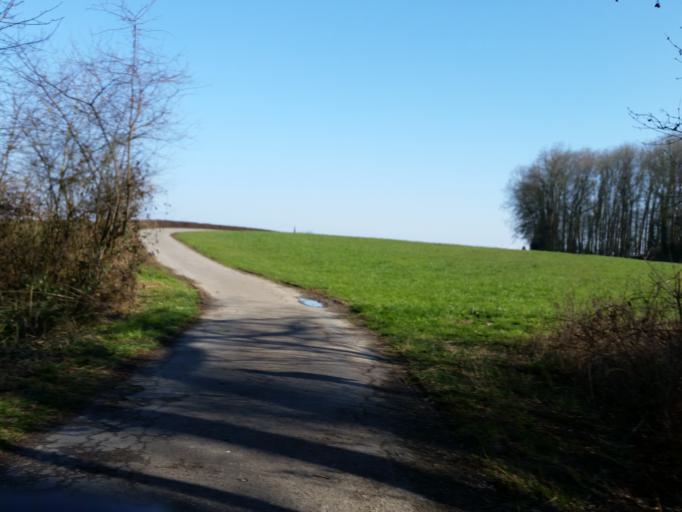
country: CH
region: Thurgau
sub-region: Arbon District
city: Uttwil
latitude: 47.5683
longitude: 9.3526
